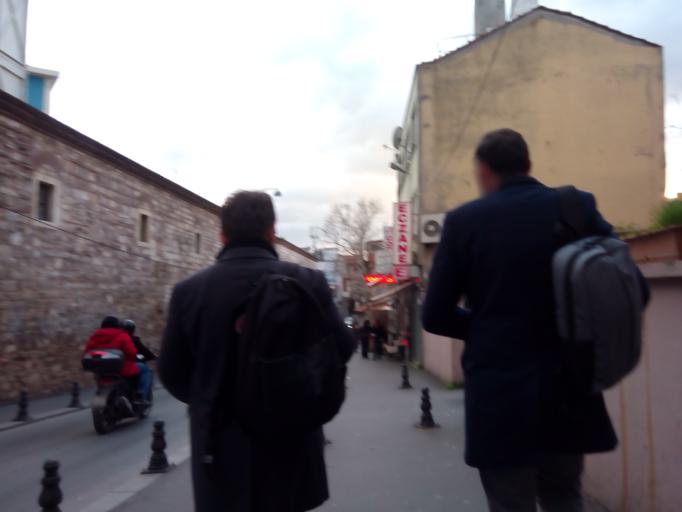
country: TR
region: Istanbul
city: Istanbul
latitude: 41.0138
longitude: 28.9617
